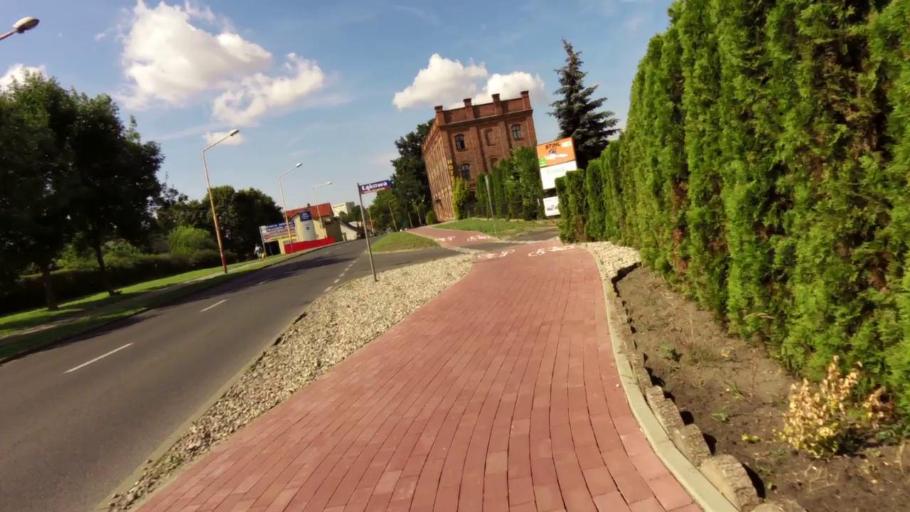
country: PL
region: West Pomeranian Voivodeship
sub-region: Powiat stargardzki
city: Stargard Szczecinski
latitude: 53.3447
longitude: 15.0560
